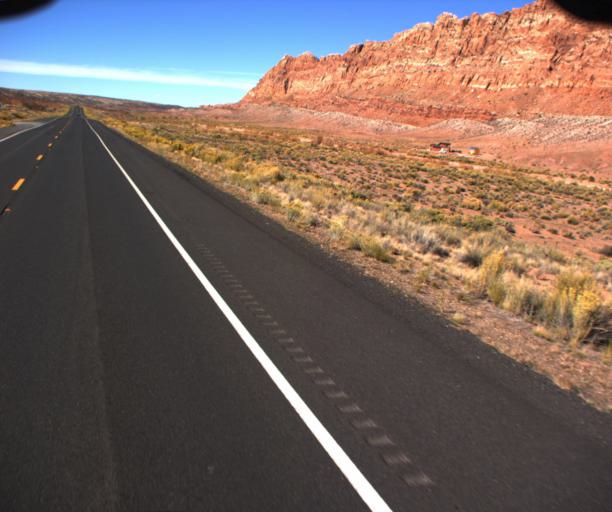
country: US
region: Arizona
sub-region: Coconino County
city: Tuba City
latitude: 36.3069
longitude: -111.4638
